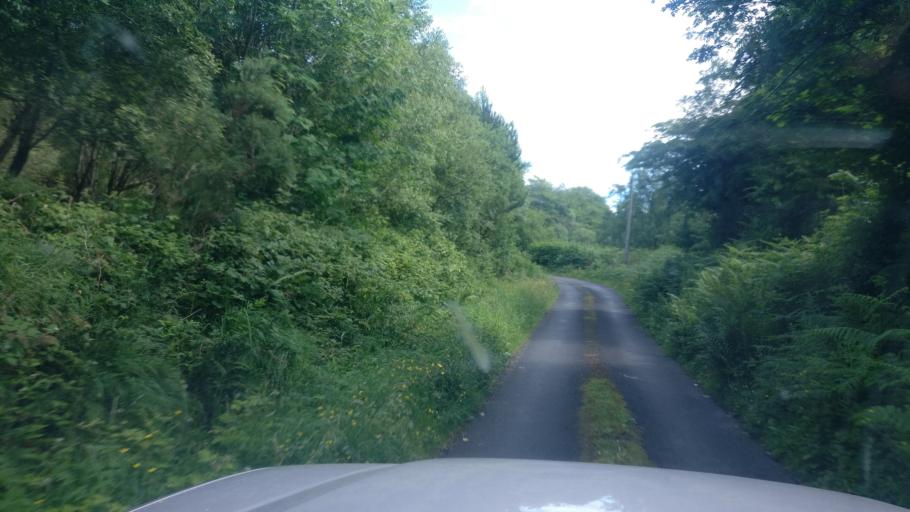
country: IE
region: Connaught
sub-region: County Galway
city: Gort
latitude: 53.0677
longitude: -8.7020
